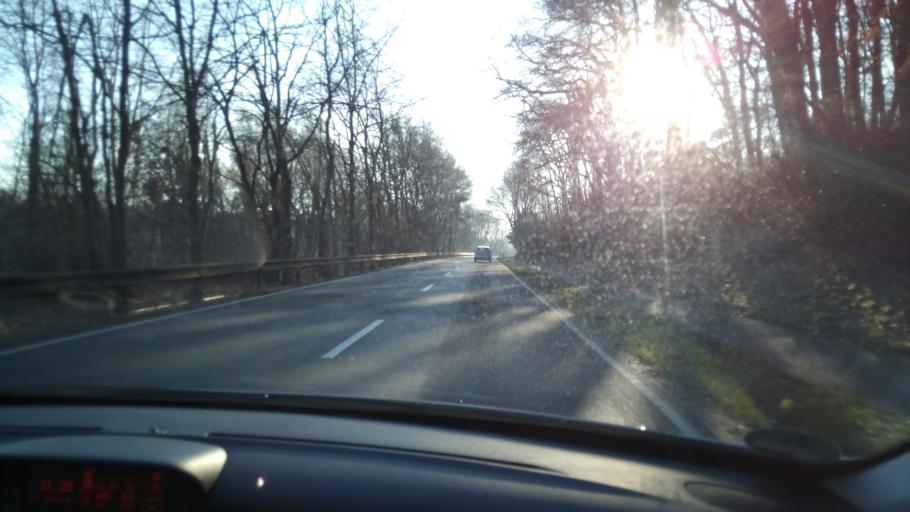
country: DE
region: Schleswig-Holstein
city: Witzeeze
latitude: 53.4645
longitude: 10.6238
